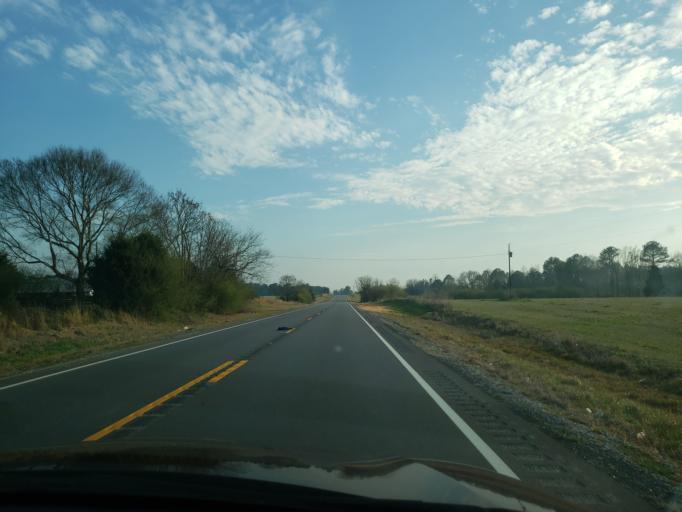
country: US
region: Alabama
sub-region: Hale County
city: Moundville
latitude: 32.8741
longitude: -87.6108
